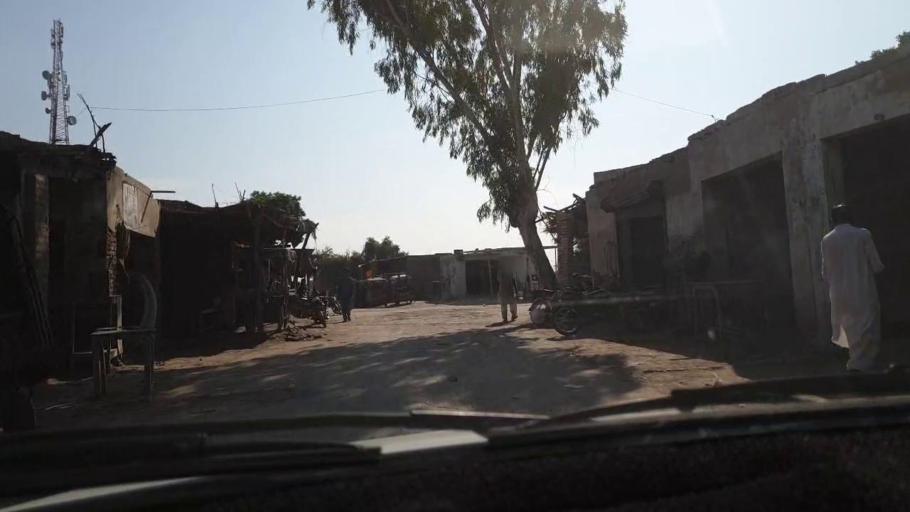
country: PK
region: Sindh
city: Bulri
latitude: 24.9594
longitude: 68.4196
